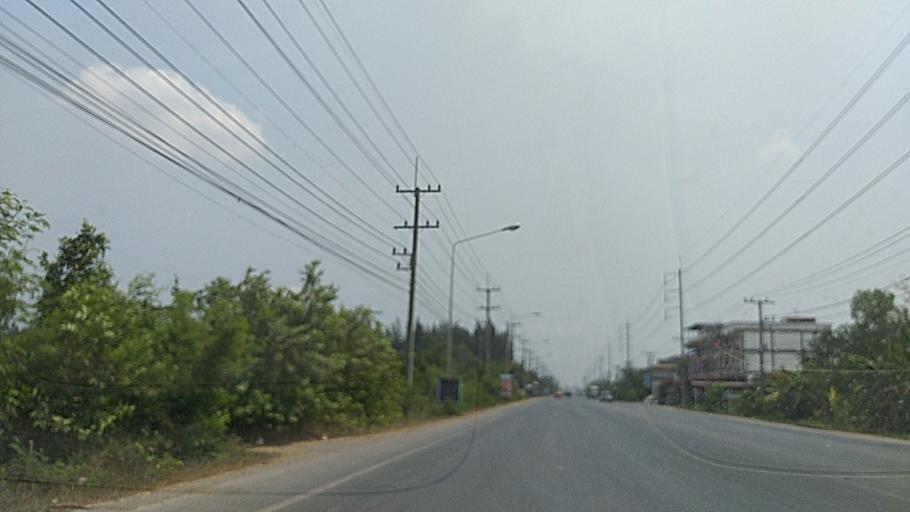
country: TH
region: Bangkok
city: Nong Chok
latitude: 13.9599
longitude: 100.8851
